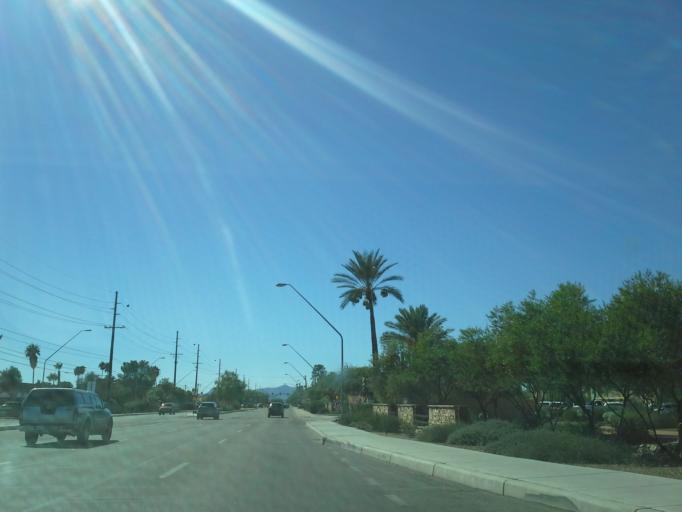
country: US
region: Arizona
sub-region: Pima County
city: Tucson
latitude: 32.2508
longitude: -110.8765
